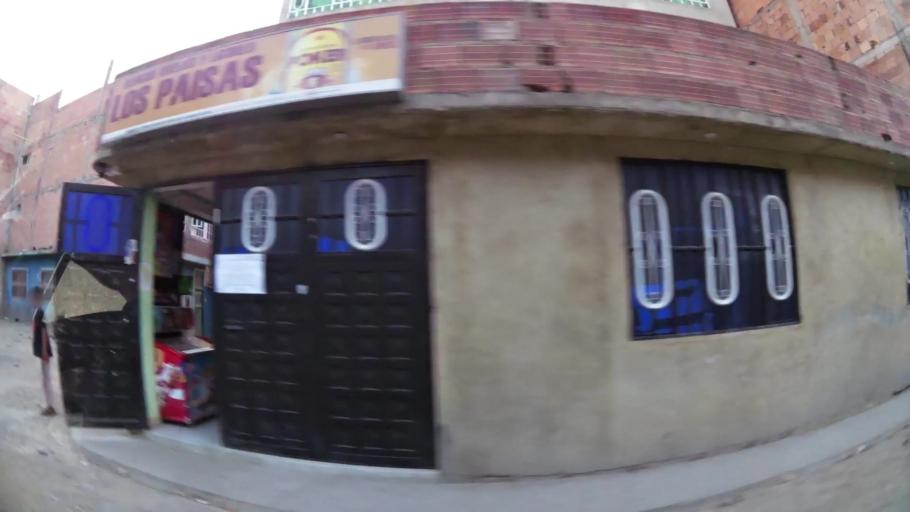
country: CO
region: Cundinamarca
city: Soacha
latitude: 4.6285
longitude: -74.1651
